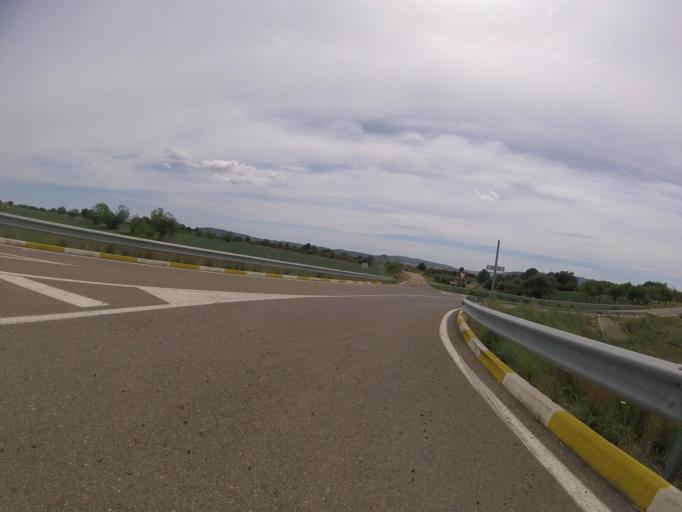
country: ES
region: Valencia
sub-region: Provincia de Castello
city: Benlloch
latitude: 40.2003
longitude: -0.0082
